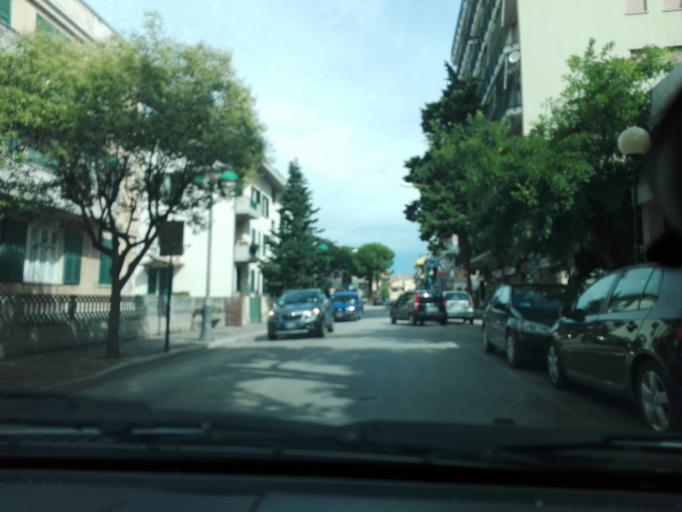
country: IT
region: Abruzzo
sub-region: Provincia di Teramo
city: Pineto
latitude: 42.6098
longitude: 14.0658
